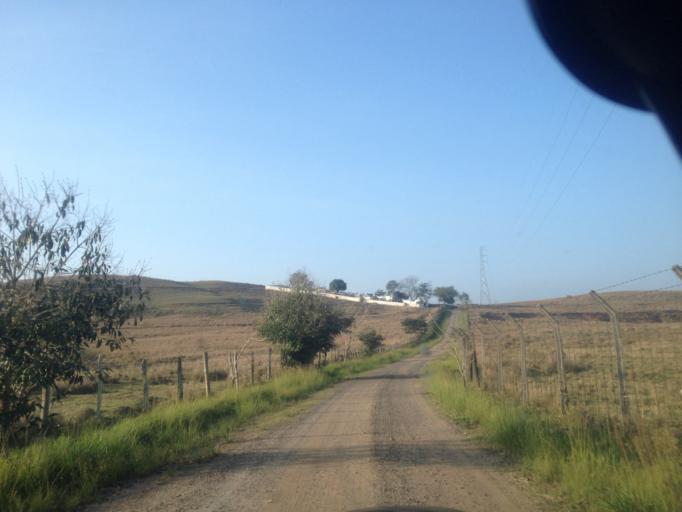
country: BR
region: Rio de Janeiro
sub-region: Porto Real
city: Porto Real
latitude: -22.4219
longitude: -44.3312
